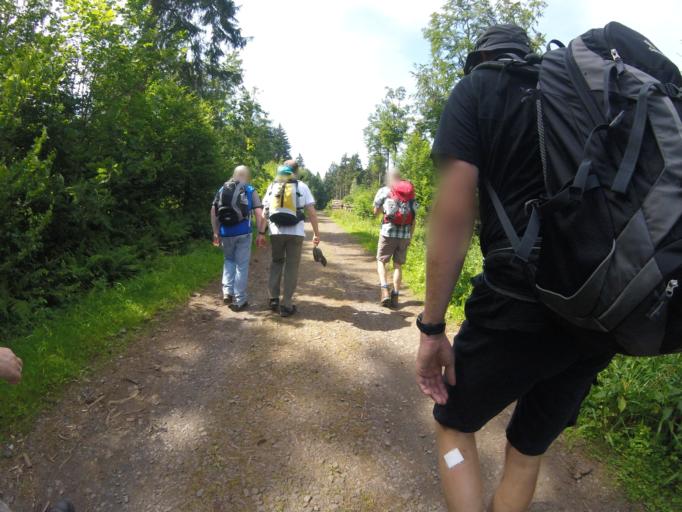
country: DE
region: Hesse
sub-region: Regierungsbezirk Giessen
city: Ulrichstein
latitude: 50.5193
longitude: 9.2380
